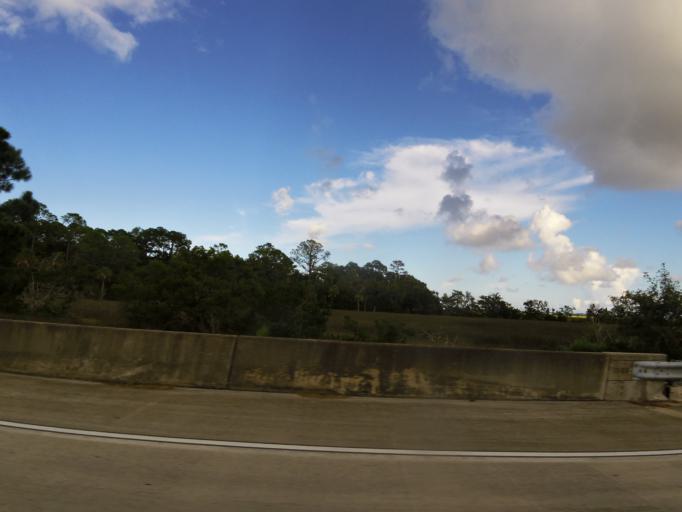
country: US
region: Georgia
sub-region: Glynn County
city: Country Club Estates
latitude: 31.1958
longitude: -81.4685
